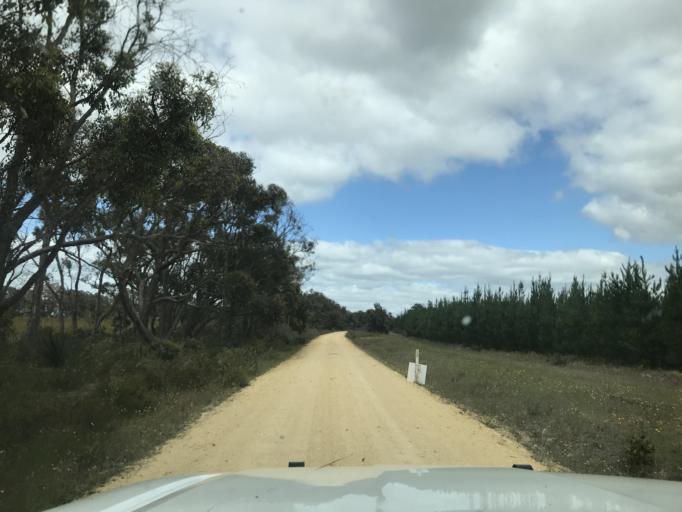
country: AU
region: South Australia
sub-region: Wattle Range
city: Penola
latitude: -37.3185
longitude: 141.1427
